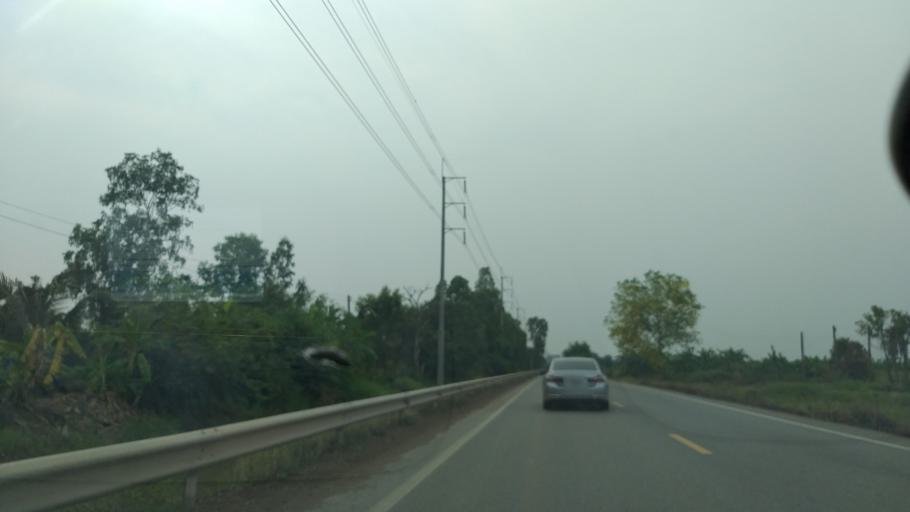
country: TH
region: Chachoengsao
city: Plaeng Yao
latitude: 13.5882
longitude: 101.2100
